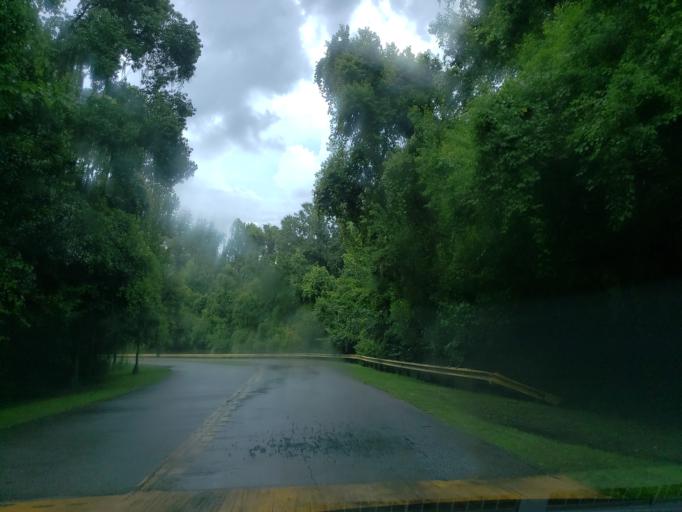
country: US
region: Georgia
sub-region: Chatham County
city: Thunderbolt
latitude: 32.0290
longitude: -81.0820
